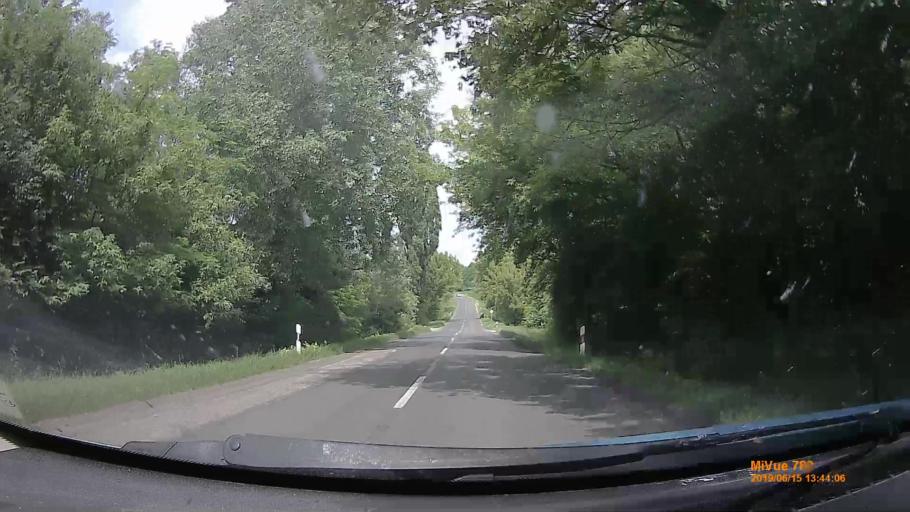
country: HU
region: Tolna
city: Iregszemcse
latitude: 46.6844
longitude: 18.1883
